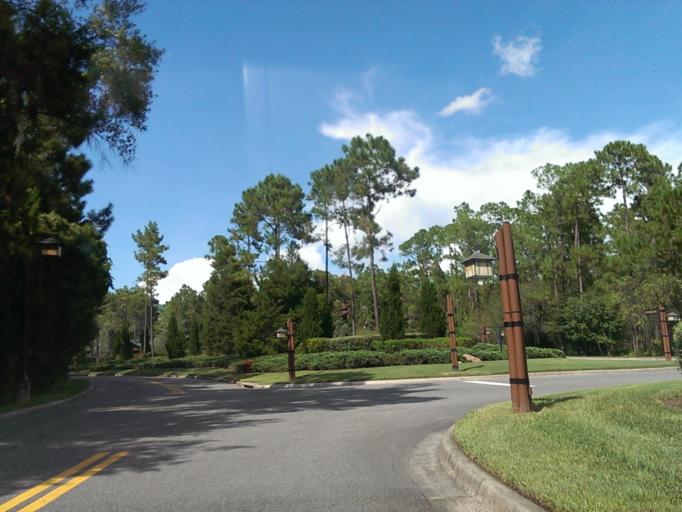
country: US
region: Florida
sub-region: Orange County
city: Bay Hill
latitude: 28.4068
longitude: -81.5731
